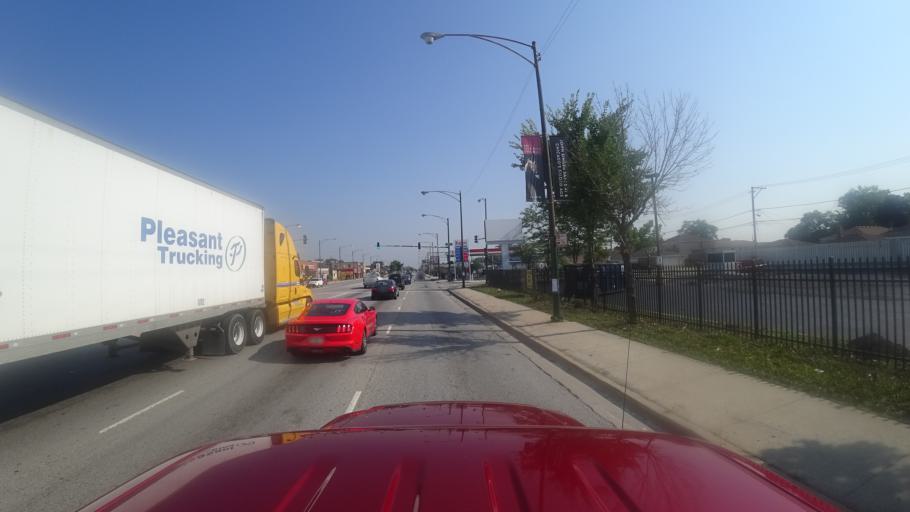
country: US
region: Illinois
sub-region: Cook County
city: Stickney
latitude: 41.8017
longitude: -87.7429
